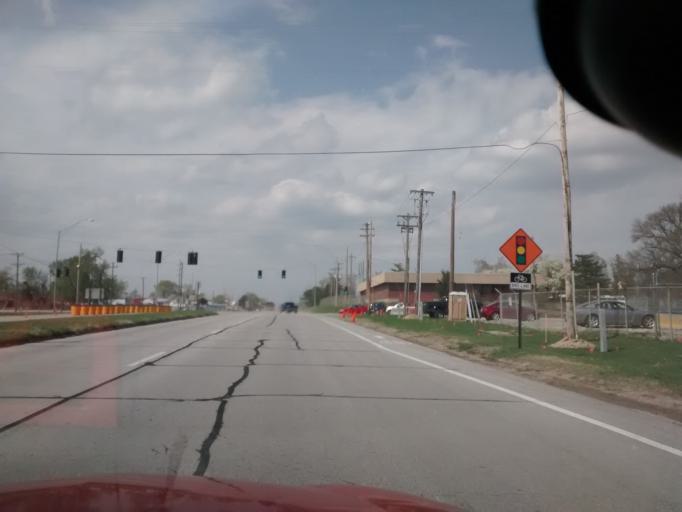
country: US
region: Nebraska
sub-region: Sarpy County
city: Offutt Air Force Base
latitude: 41.1178
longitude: -95.9265
